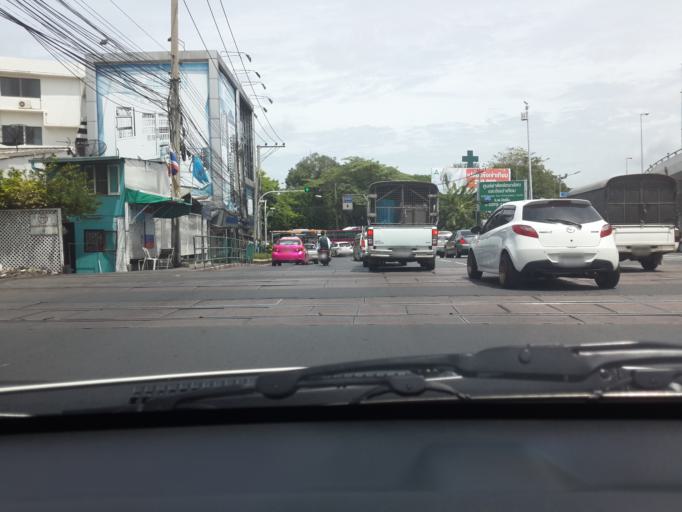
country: TH
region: Bangkok
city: Pom Prap Sattru Phai
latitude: 13.7568
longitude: 100.5209
